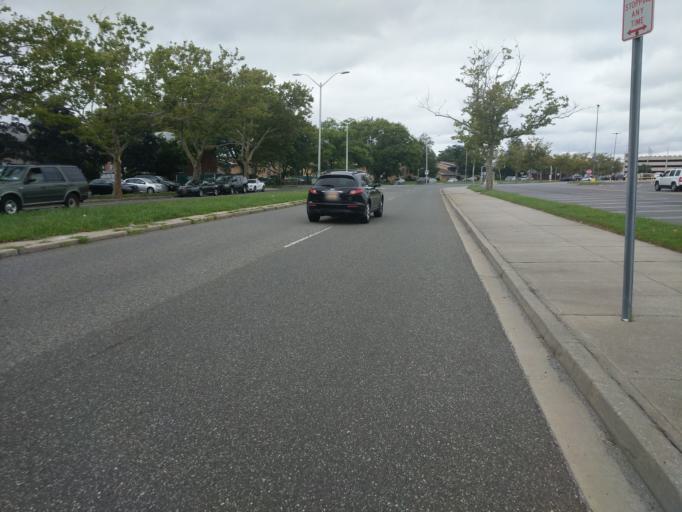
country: US
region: New York
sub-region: Nassau County
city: South Valley Stream
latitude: 40.6607
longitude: -73.7173
